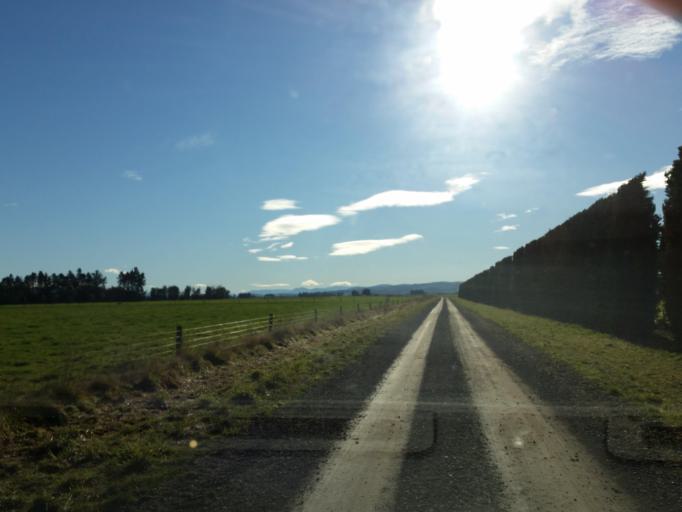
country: NZ
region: Southland
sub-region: Southland District
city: Winton
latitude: -46.1068
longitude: 168.1143
